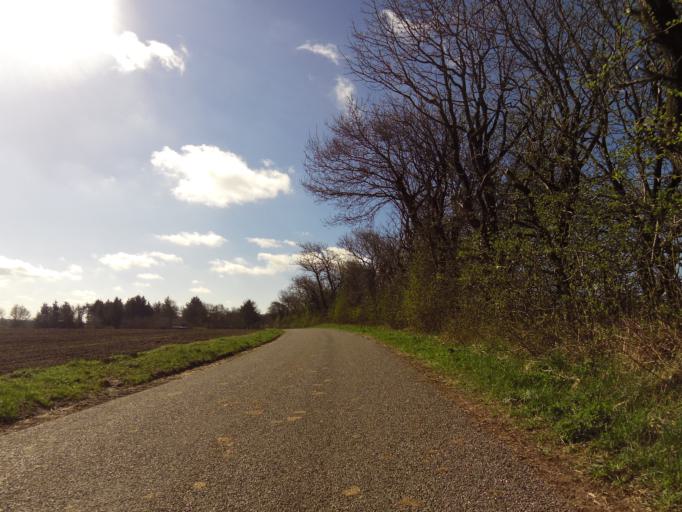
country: DK
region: Central Jutland
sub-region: Holstebro Kommune
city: Vinderup
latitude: 56.4391
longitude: 8.7246
